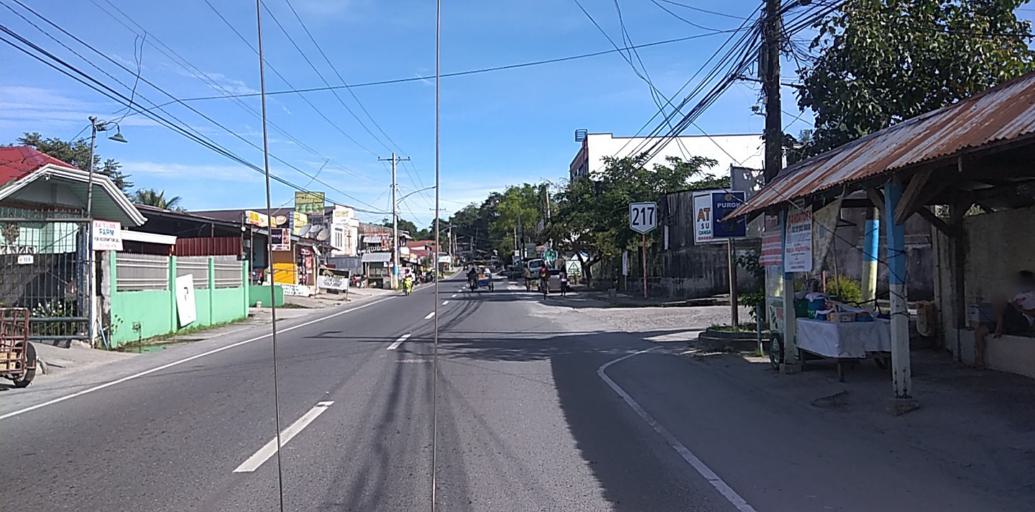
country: PH
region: Central Luzon
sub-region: Province of Pampanga
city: Porac
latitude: 15.0750
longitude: 120.5434
